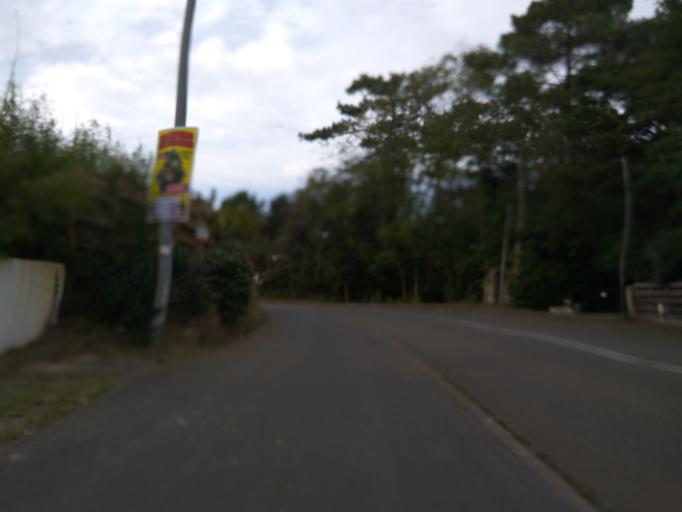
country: FR
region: Aquitaine
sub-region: Departement des Landes
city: Capbreton
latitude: 43.6393
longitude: -1.4373
